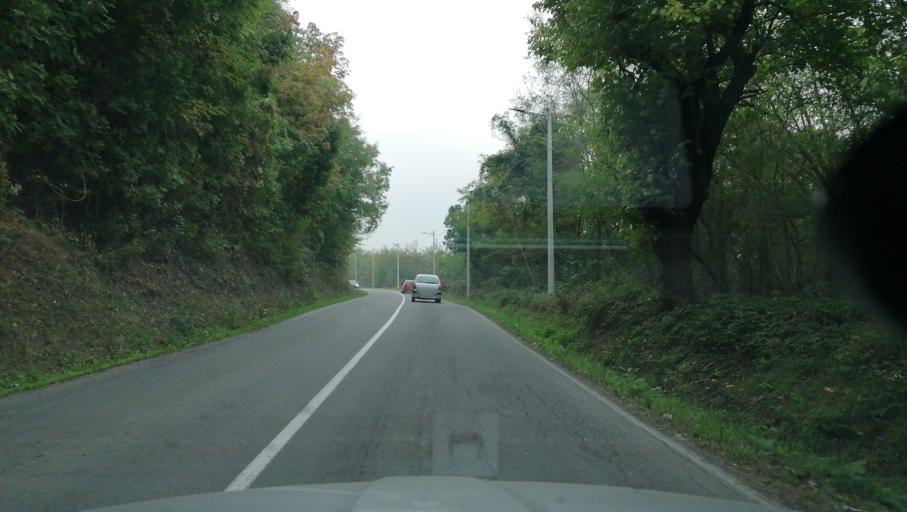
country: RS
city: Rusanj
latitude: 44.6856
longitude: 20.5050
